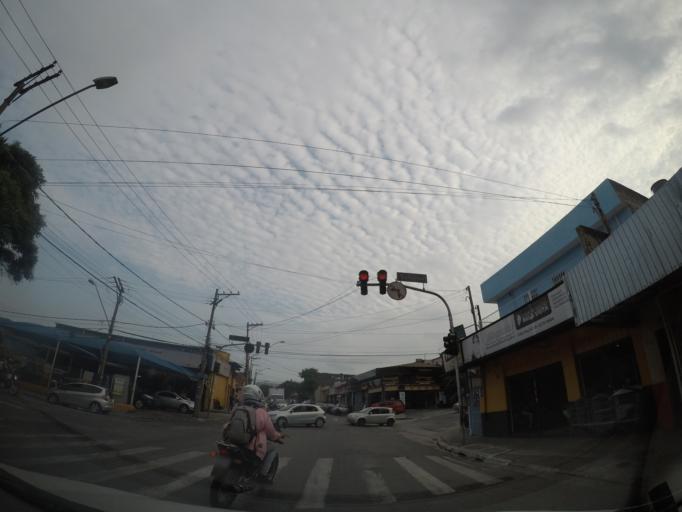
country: BR
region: Sao Paulo
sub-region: Guarulhos
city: Guarulhos
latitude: -23.4322
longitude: -46.5090
